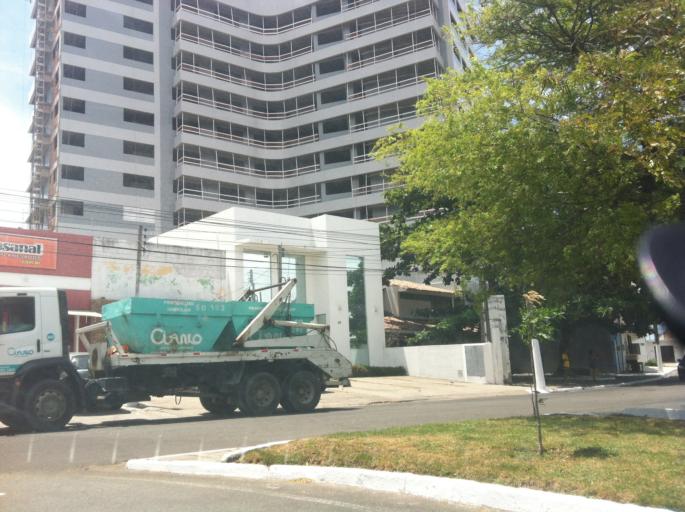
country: BR
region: Alagoas
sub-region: Maceio
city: Maceio
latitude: -9.6732
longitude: -35.7188
